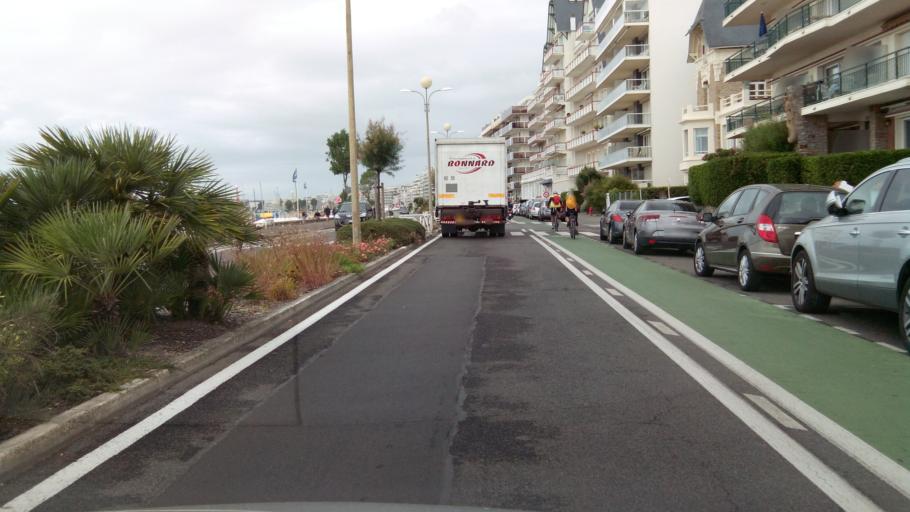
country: FR
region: Pays de la Loire
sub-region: Departement de la Loire-Atlantique
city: La Baule-Escoublac
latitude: 47.2808
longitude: -2.3841
